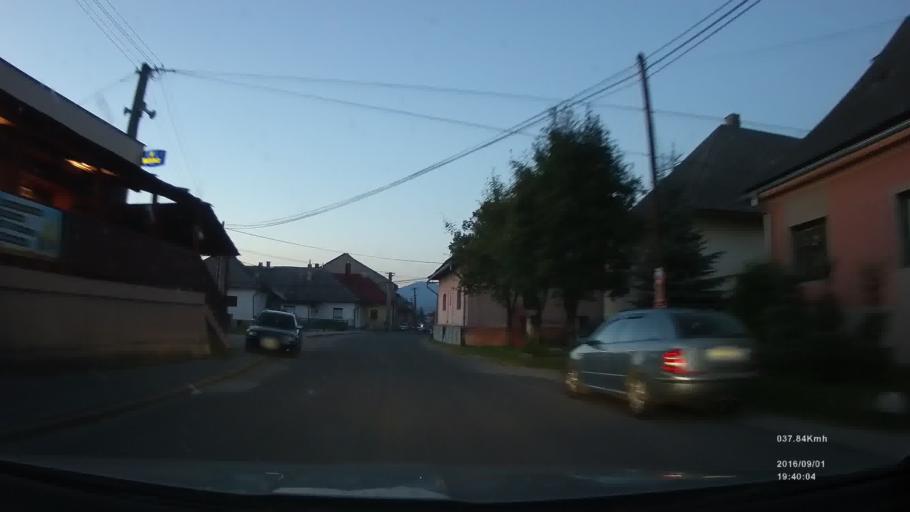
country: SK
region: Zilinsky
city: Ruzomberok
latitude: 49.0590
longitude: 19.4318
